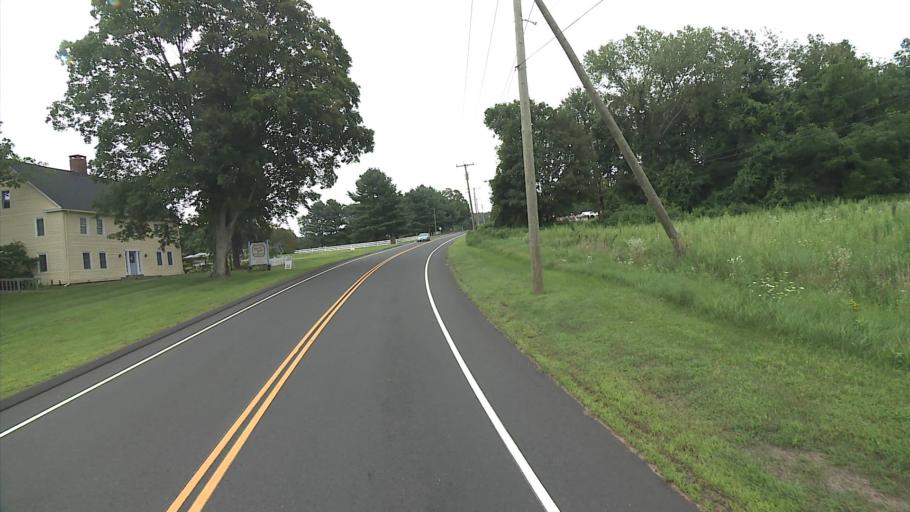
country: US
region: Connecticut
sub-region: Tolland County
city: Rockville
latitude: 41.8704
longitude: -72.4129
